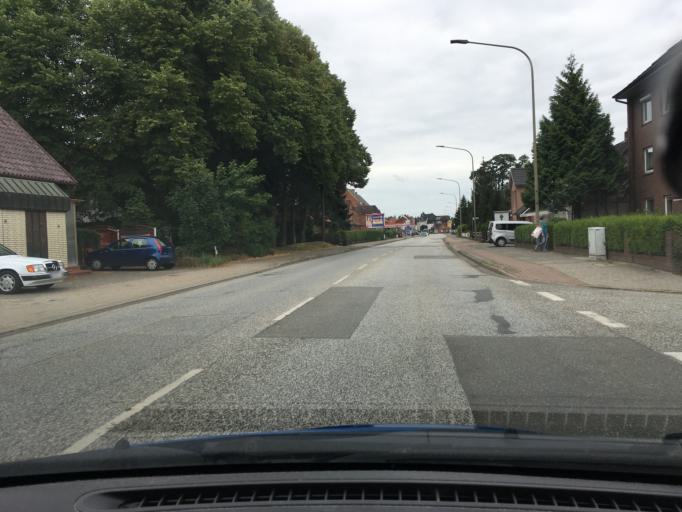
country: DE
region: Schleswig-Holstein
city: Geesthacht
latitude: 53.4464
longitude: 10.3617
